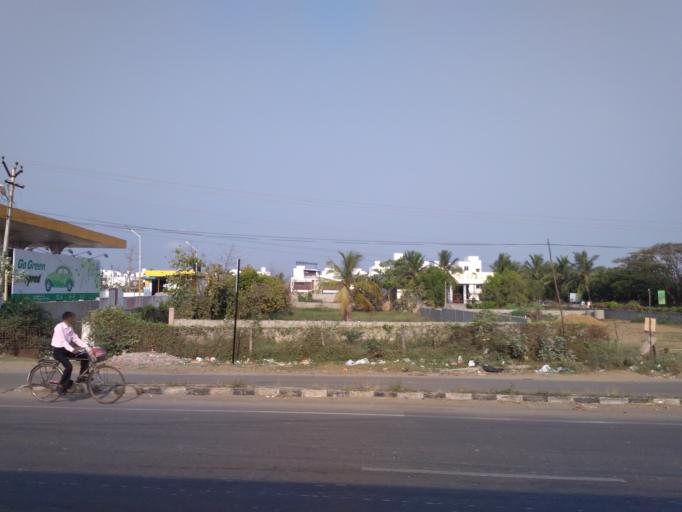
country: IN
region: Tamil Nadu
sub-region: Kancheepuram
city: Injambakkam
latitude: 12.8155
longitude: 80.2294
